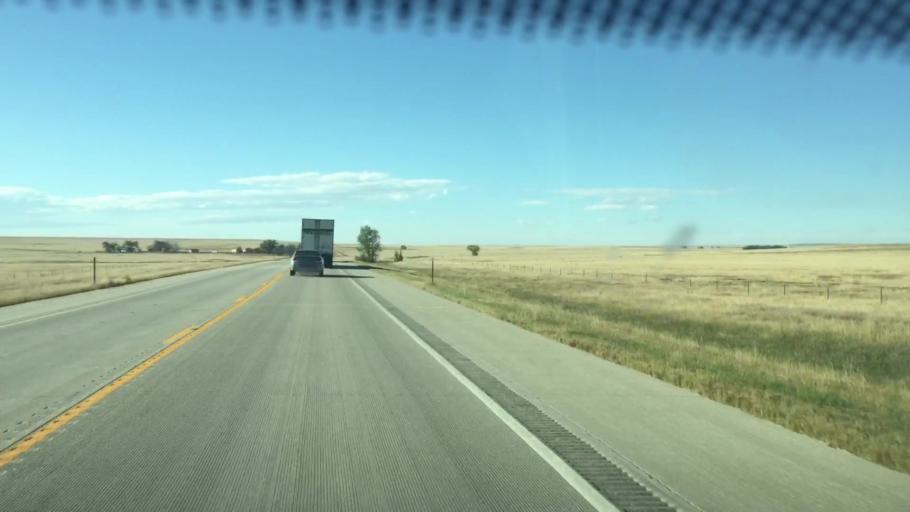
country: US
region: Colorado
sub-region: Lincoln County
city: Hugo
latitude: 38.9297
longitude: -103.1966
